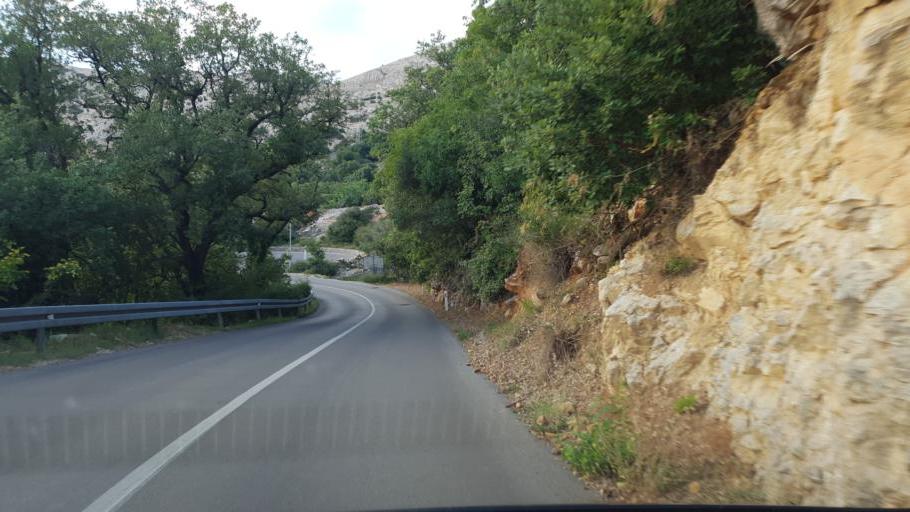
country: HR
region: Primorsko-Goranska
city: Punat
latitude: 44.9645
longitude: 14.6799
